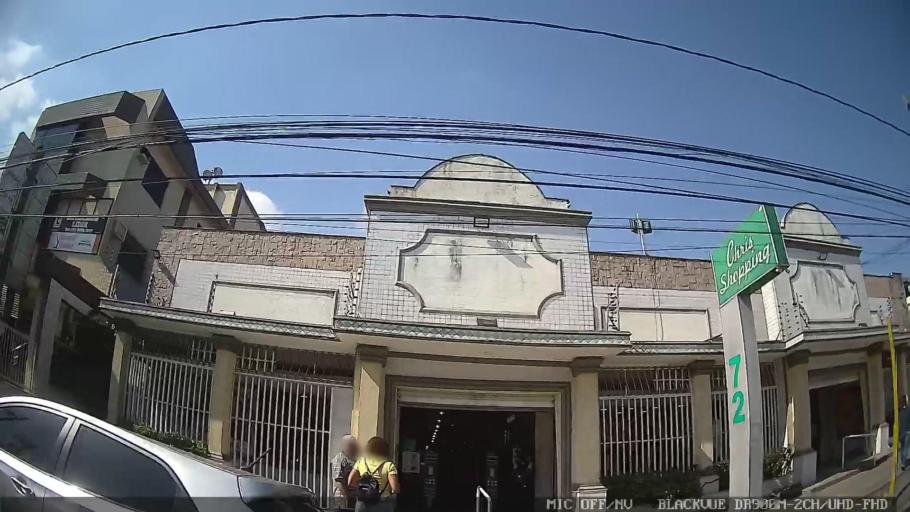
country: BR
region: Sao Paulo
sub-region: Santos
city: Santos
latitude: -23.9425
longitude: -46.3002
